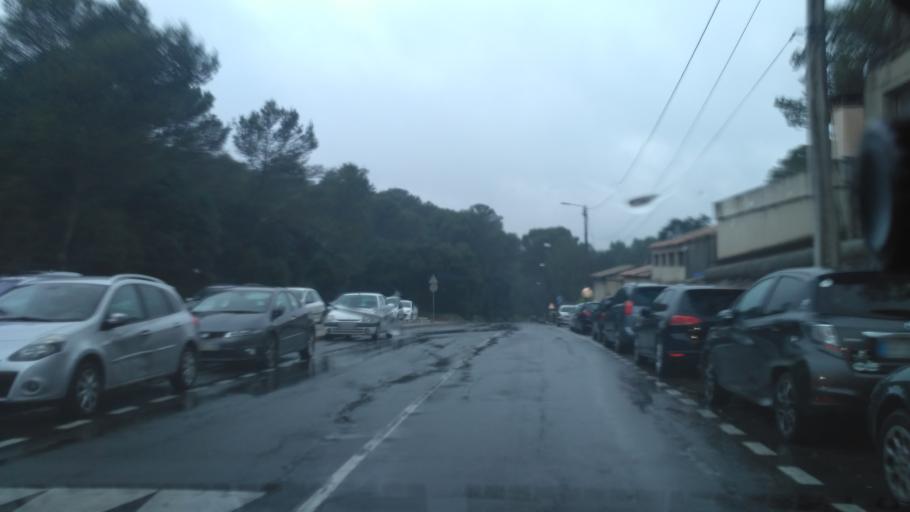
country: FR
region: Languedoc-Roussillon
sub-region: Departement de l'Herault
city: Clapiers
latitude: 43.6405
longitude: 3.8728
